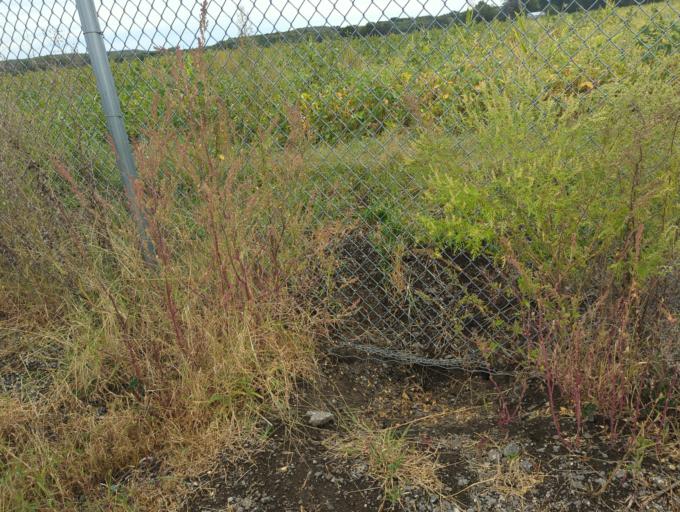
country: US
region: Kansas
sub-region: Douglas County
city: Lawrence
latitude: 39.0071
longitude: -95.2098
